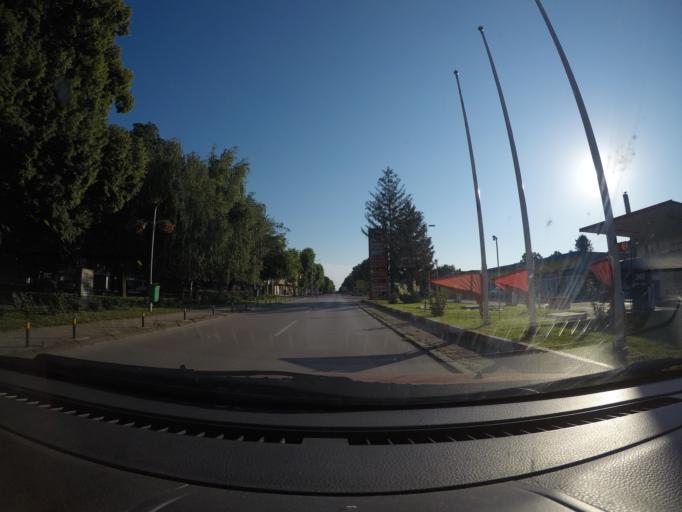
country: RS
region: Central Serbia
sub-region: Branicevski Okrug
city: Veliko Gradiste
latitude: 44.7622
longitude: 21.5147
